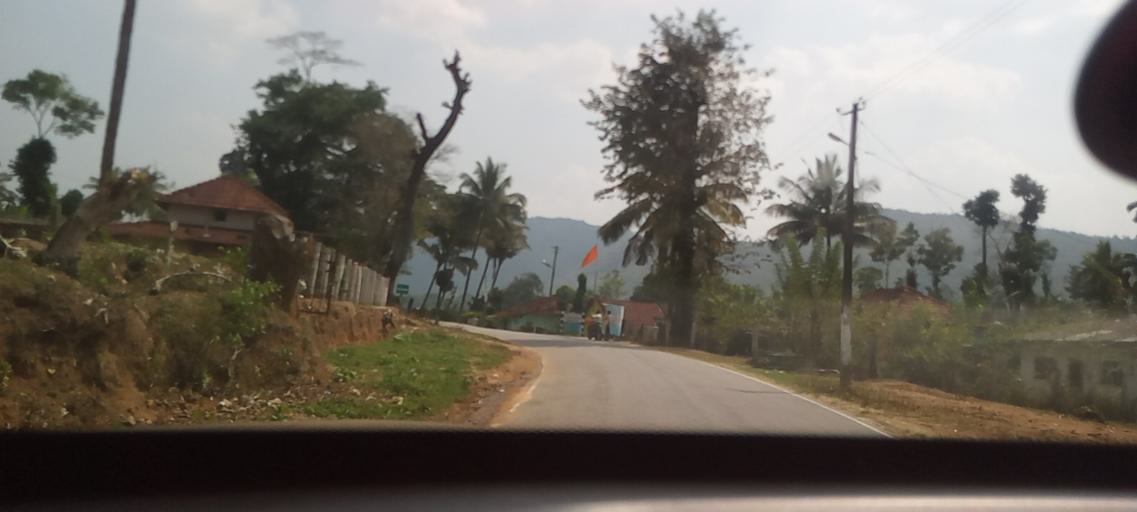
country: IN
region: Karnataka
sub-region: Chikmagalur
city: Mudigere
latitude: 13.2976
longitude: 75.5920
